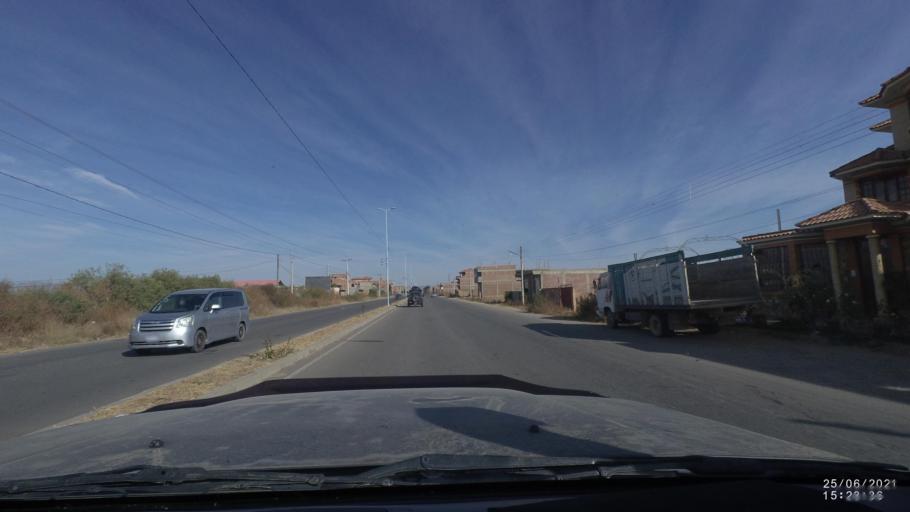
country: BO
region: Cochabamba
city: Cliza
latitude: -17.5613
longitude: -65.9365
